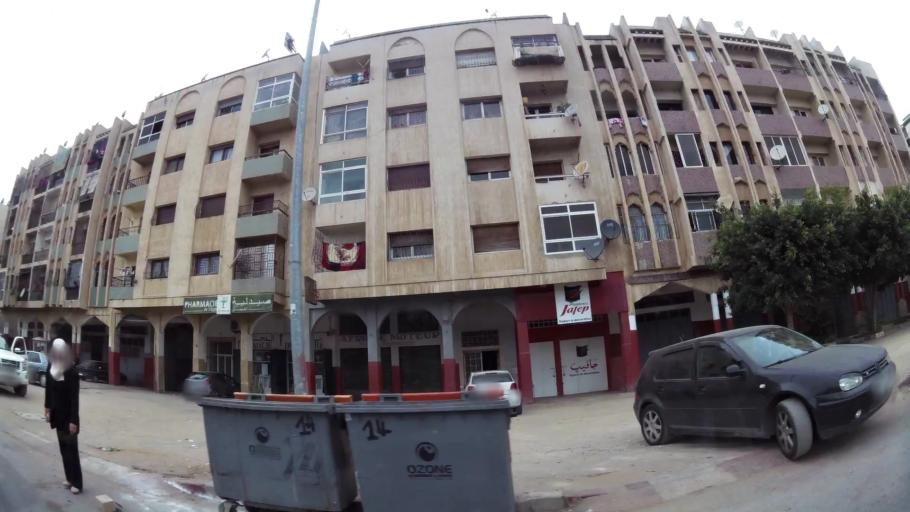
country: MA
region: Rabat-Sale-Zemmour-Zaer
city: Sale
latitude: 34.0366
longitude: -6.8017
